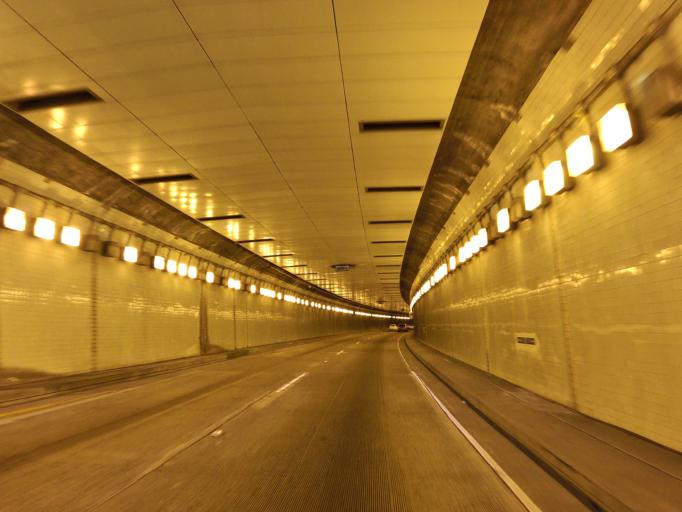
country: US
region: California
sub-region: Contra Costa County
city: Orinda
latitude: 37.8610
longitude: -122.2104
